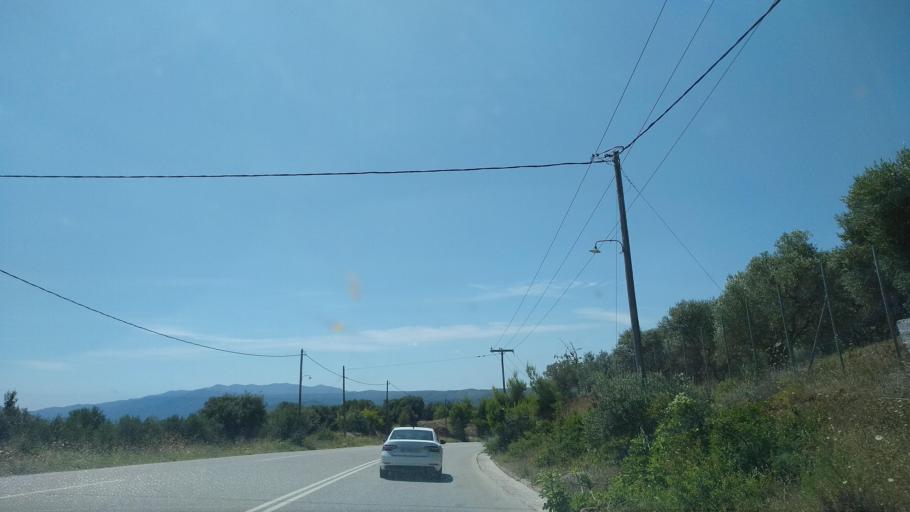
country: GR
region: Central Macedonia
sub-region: Nomos Chalkidikis
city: Agios Nikolaos
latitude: 40.2649
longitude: 23.6976
